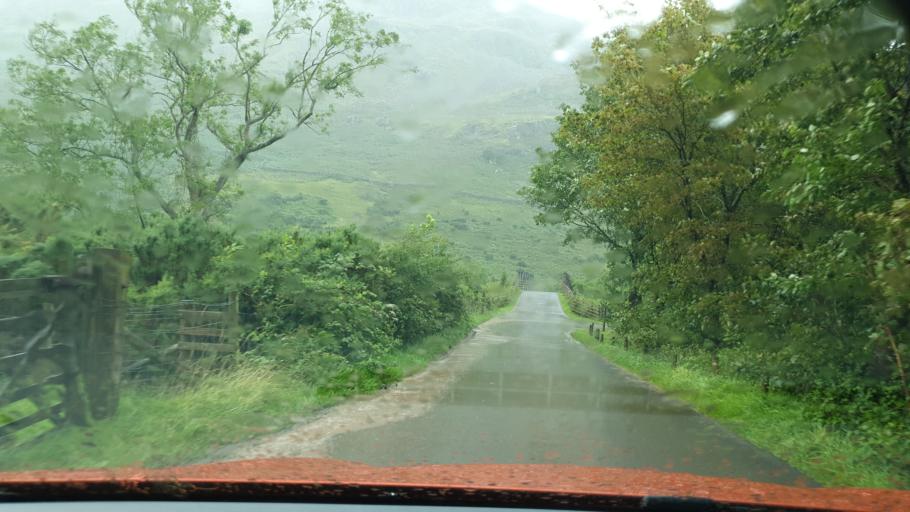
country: GB
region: England
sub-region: Cumbria
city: Keswick
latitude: 54.4563
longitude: -3.2638
